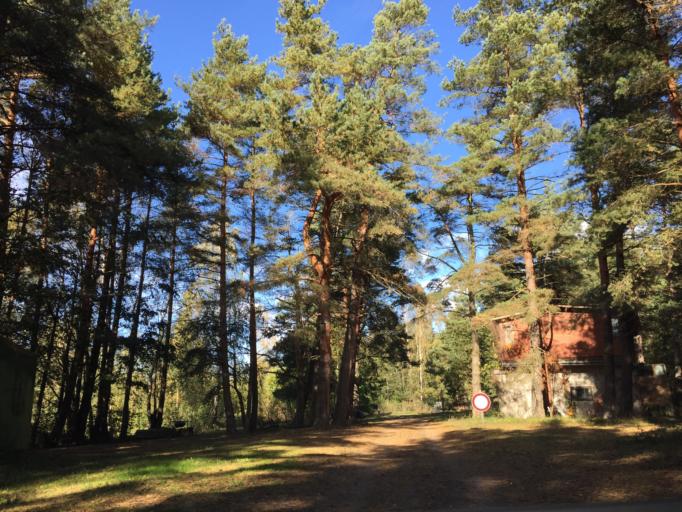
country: LV
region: Mesraga
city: Mersrags
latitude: 57.2593
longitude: 23.1356
